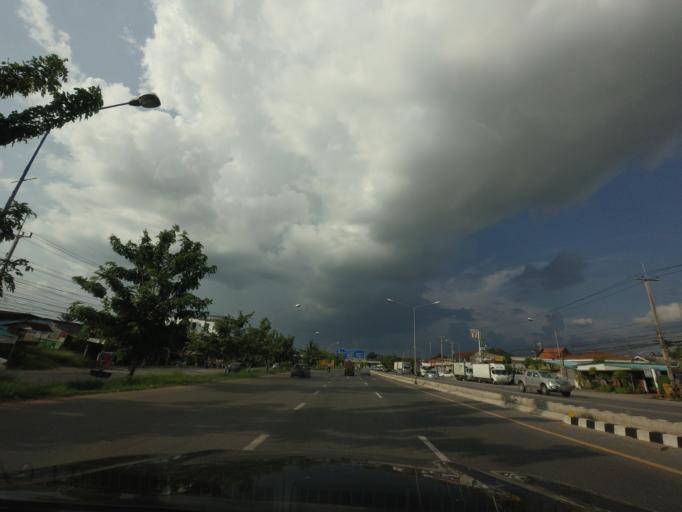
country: TH
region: Khon Kaen
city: Khon Kaen
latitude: 16.3242
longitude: 102.7962
